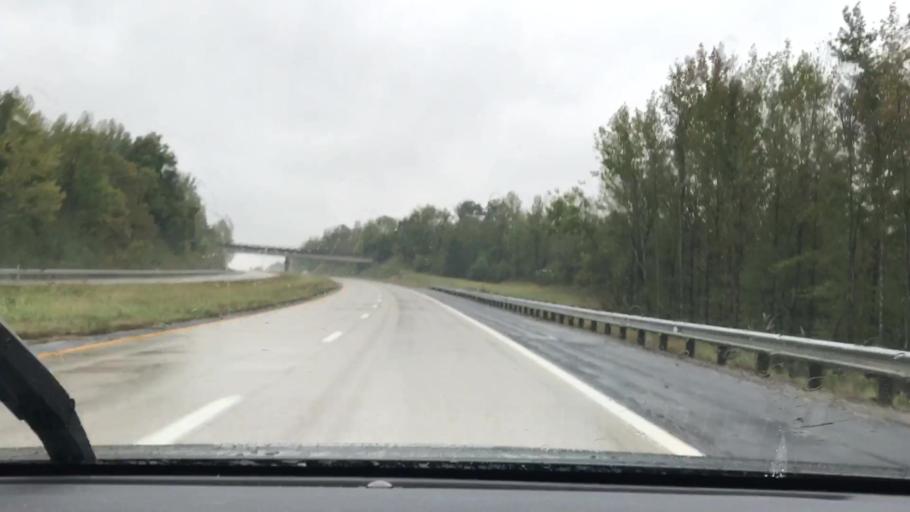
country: US
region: Kentucky
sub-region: Hopkins County
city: Nortonville
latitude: 37.1449
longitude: -87.4649
